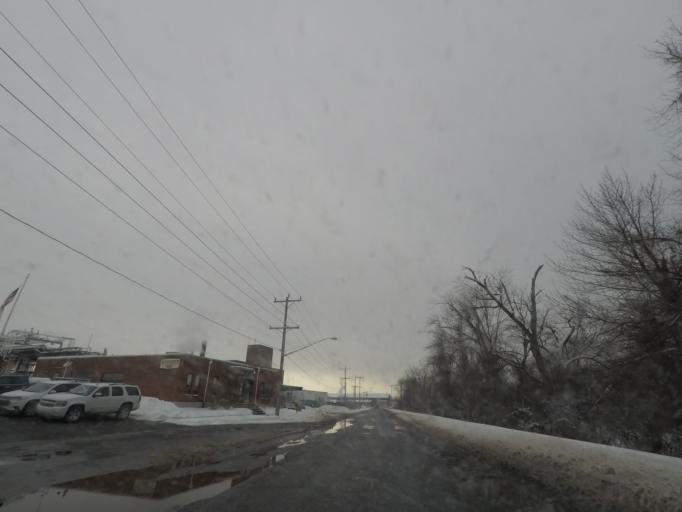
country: US
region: New York
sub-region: Rensselaer County
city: Rensselaer
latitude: 42.6177
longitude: -73.7640
